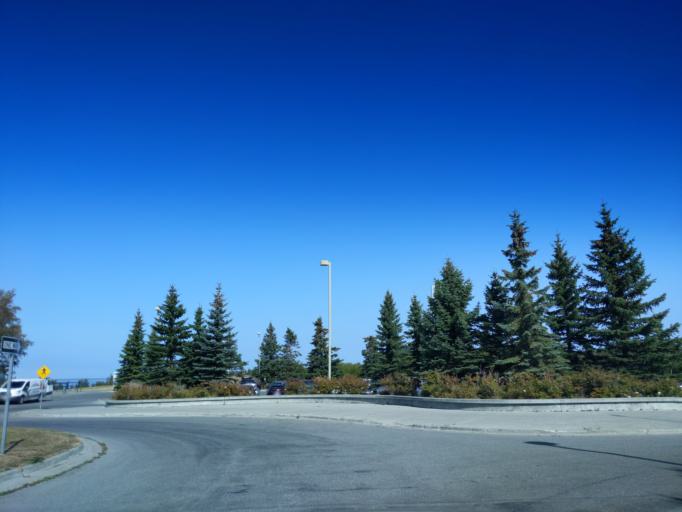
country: US
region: Alaska
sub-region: Anchorage Municipality
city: Anchorage
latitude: 61.1536
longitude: -150.0546
